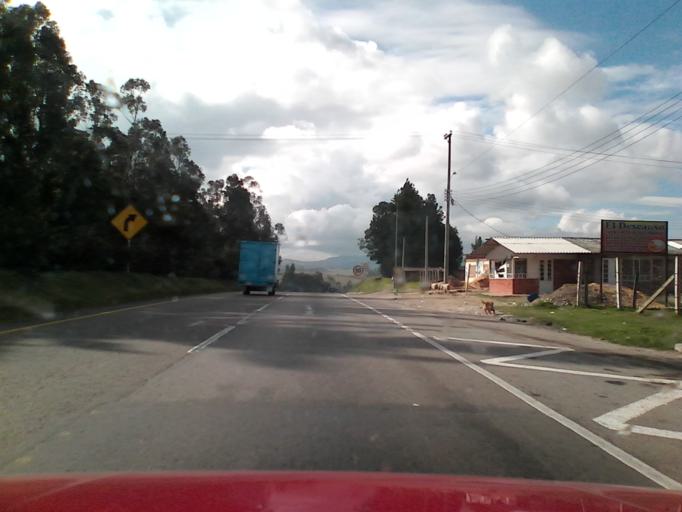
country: CO
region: Boyaca
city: Tuta
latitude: 5.6732
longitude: -73.2696
